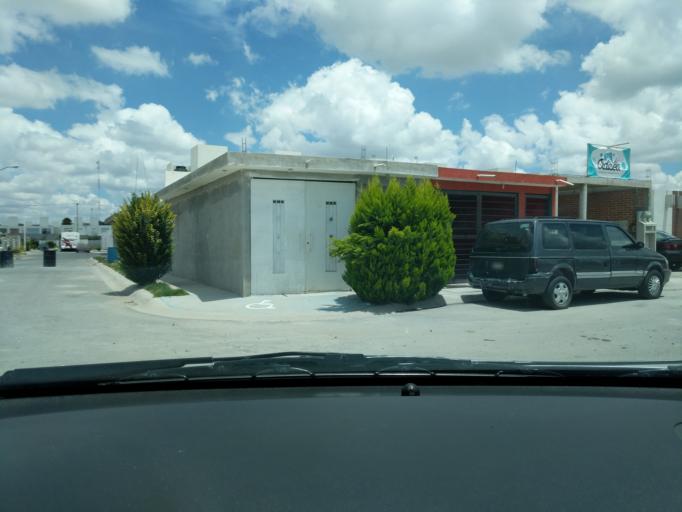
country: MX
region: San Luis Potosi
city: Soledad Diez Gutierrez
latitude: 22.2174
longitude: -100.9342
